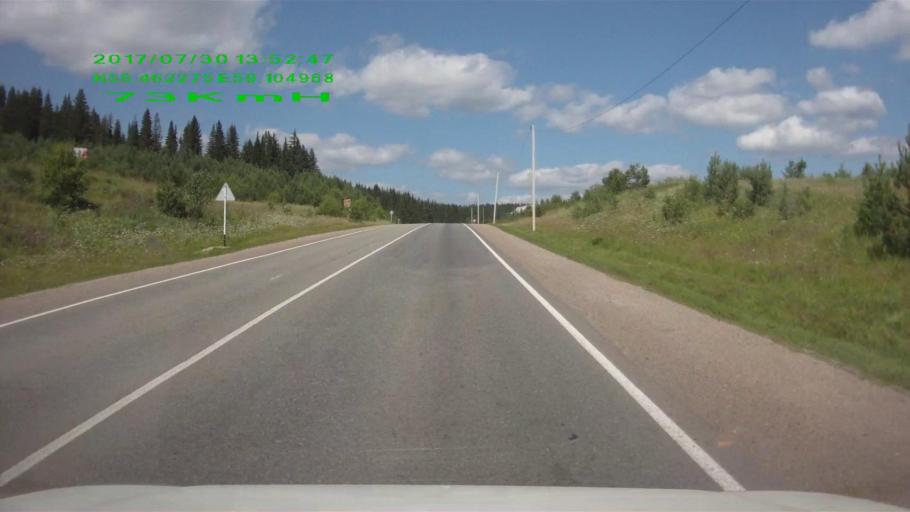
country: RU
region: Sverdlovsk
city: Mikhaylovsk
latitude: 56.4629
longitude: 59.1057
